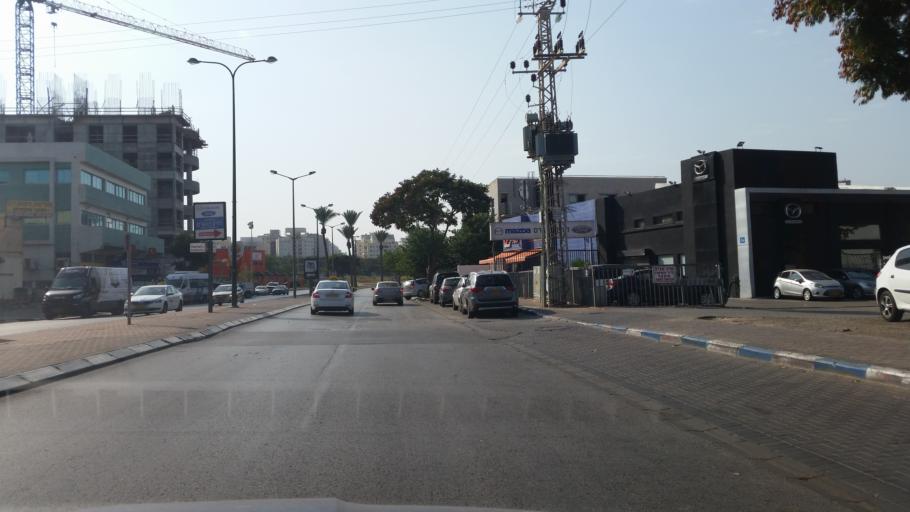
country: IL
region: Central District
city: Bet Yizhaq
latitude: 32.3149
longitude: 34.8736
